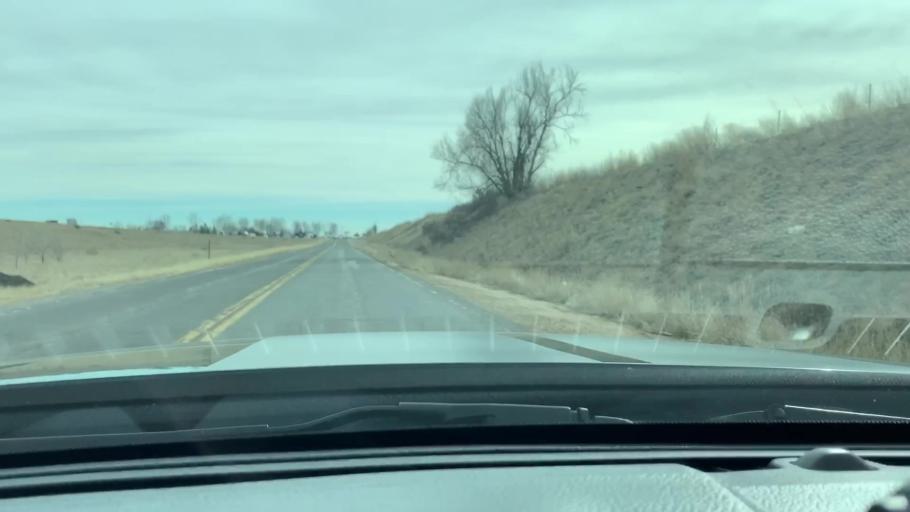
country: US
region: Colorado
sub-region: Weld County
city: Johnstown
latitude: 40.3631
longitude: -104.9866
